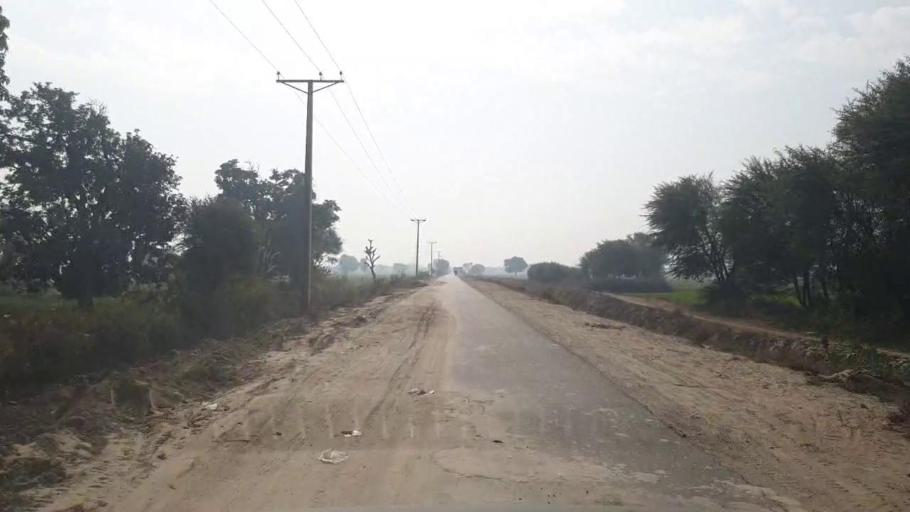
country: PK
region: Sindh
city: Hala
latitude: 25.7904
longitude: 68.4404
